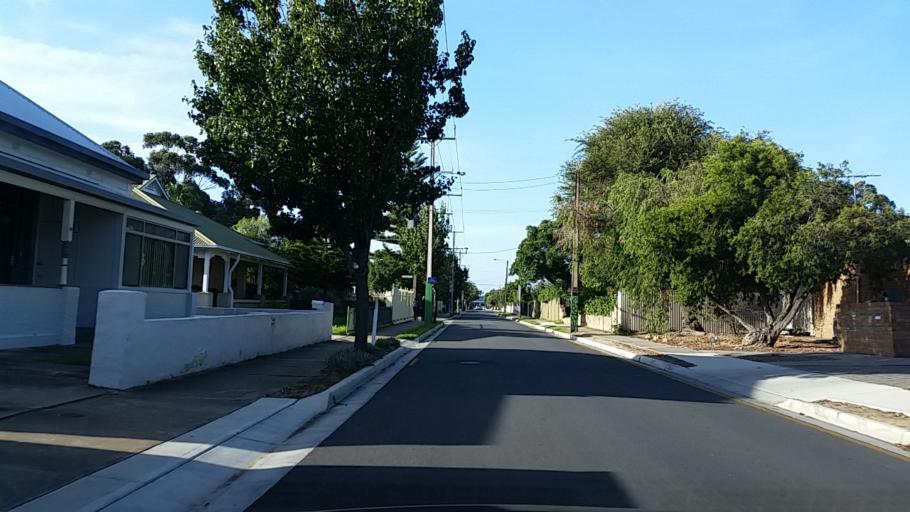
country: AU
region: South Australia
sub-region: Charles Sturt
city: Woodville
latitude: -34.8841
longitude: 138.5547
